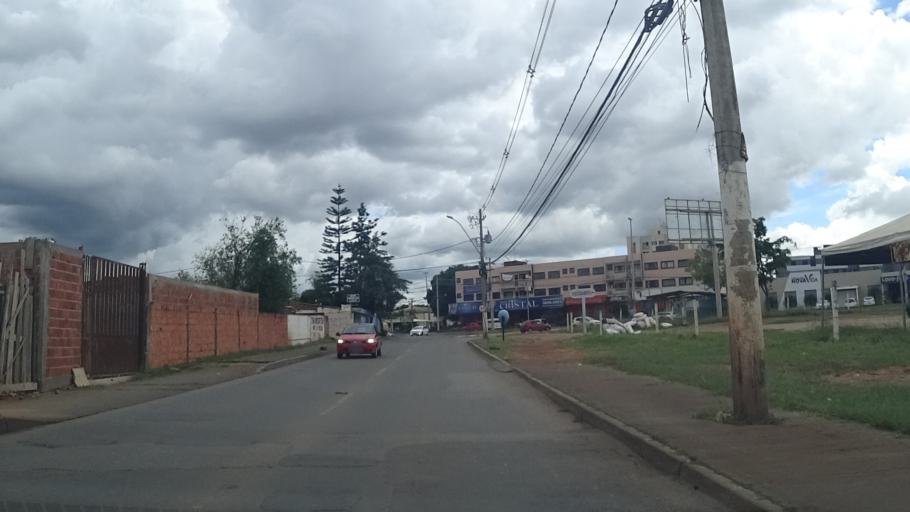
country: BR
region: Federal District
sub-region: Brasilia
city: Brasilia
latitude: -15.8535
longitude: -48.0304
